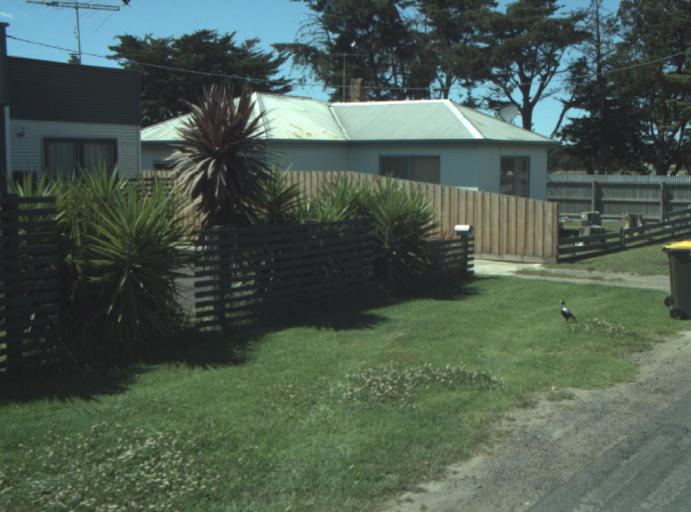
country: AU
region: Victoria
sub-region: Greater Geelong
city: Breakwater
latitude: -38.1911
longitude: 144.3536
